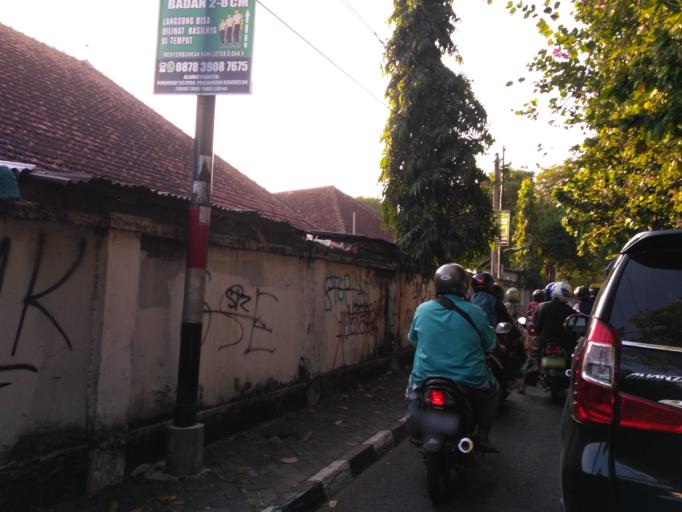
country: ID
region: Daerah Istimewa Yogyakarta
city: Yogyakarta
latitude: -7.8025
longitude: 110.3806
